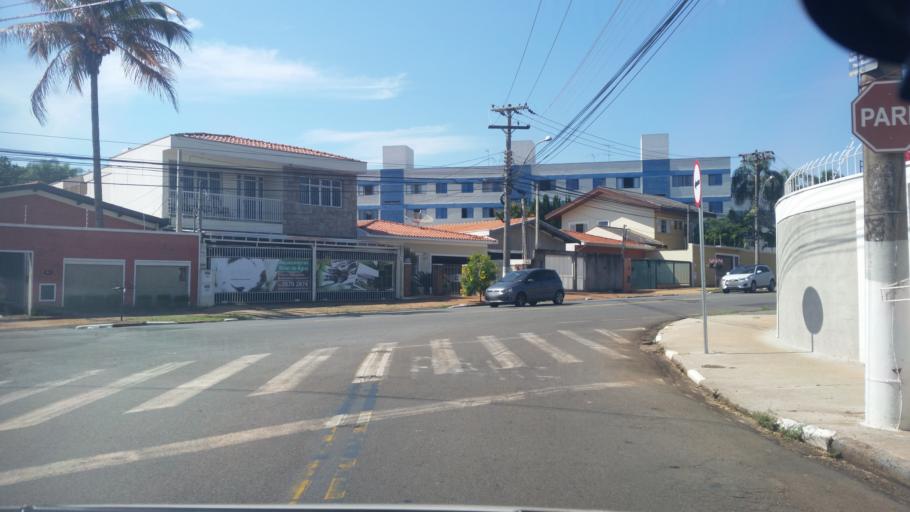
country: BR
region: Sao Paulo
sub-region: Campinas
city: Campinas
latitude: -22.8707
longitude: -47.0647
